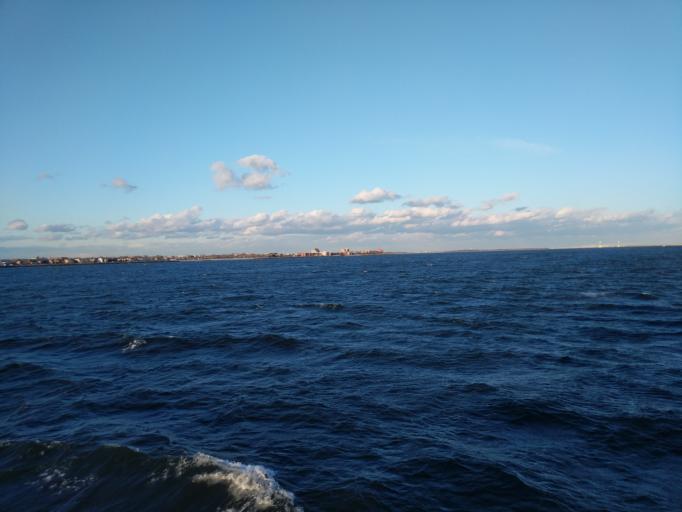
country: US
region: New York
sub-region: Kings County
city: Coney Island
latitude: 40.5644
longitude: -73.9557
